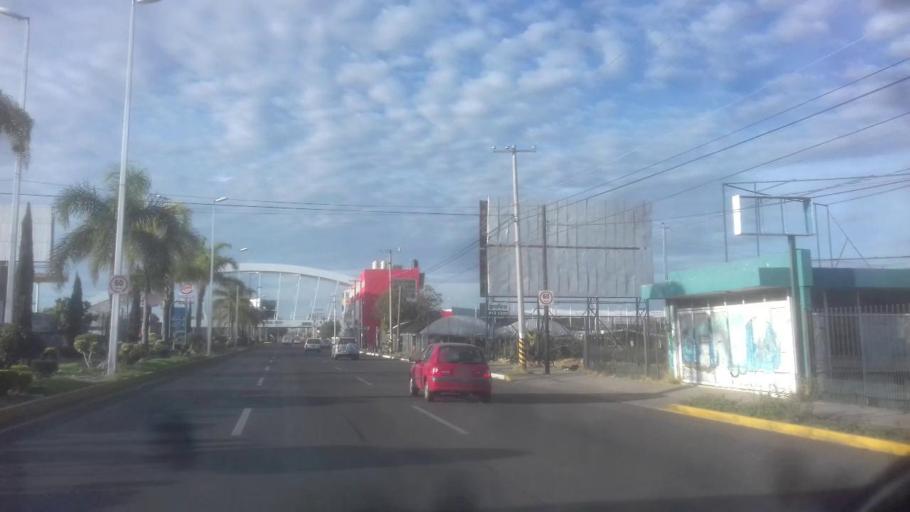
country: MX
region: Aguascalientes
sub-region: Aguascalientes
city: Aguascalientes
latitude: 21.8608
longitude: -102.2935
